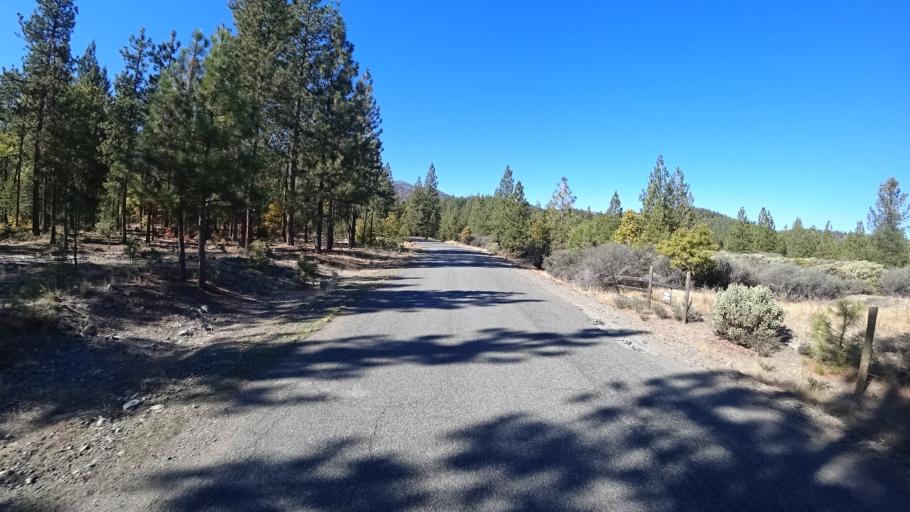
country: US
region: California
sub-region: Siskiyou County
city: Yreka
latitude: 41.5122
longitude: -122.9182
